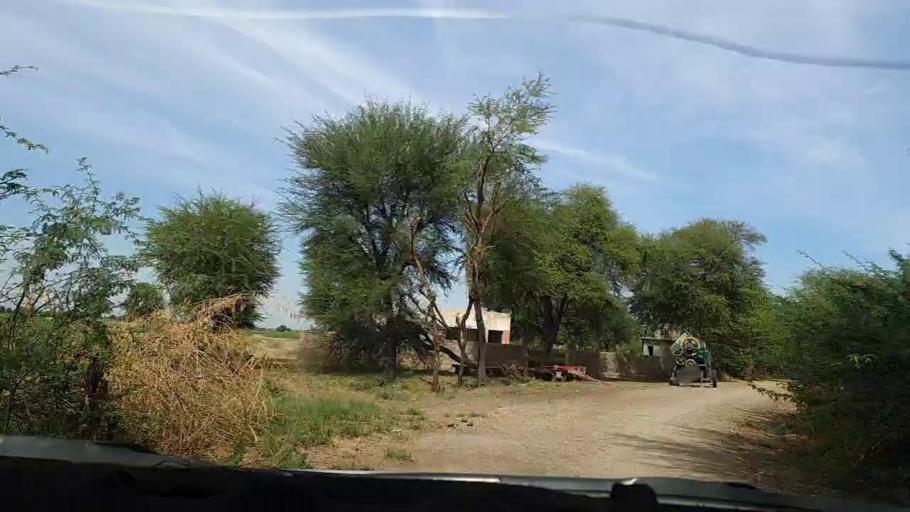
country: PK
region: Sindh
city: Dhoro Naro
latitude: 25.4604
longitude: 69.4775
